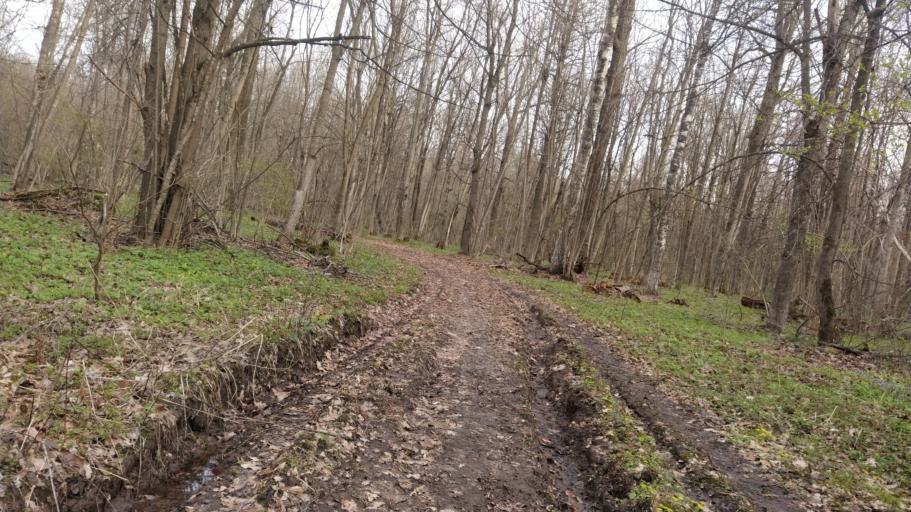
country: RU
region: Chuvashia
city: Novyye Lapsary
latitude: 56.1367
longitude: 47.1182
